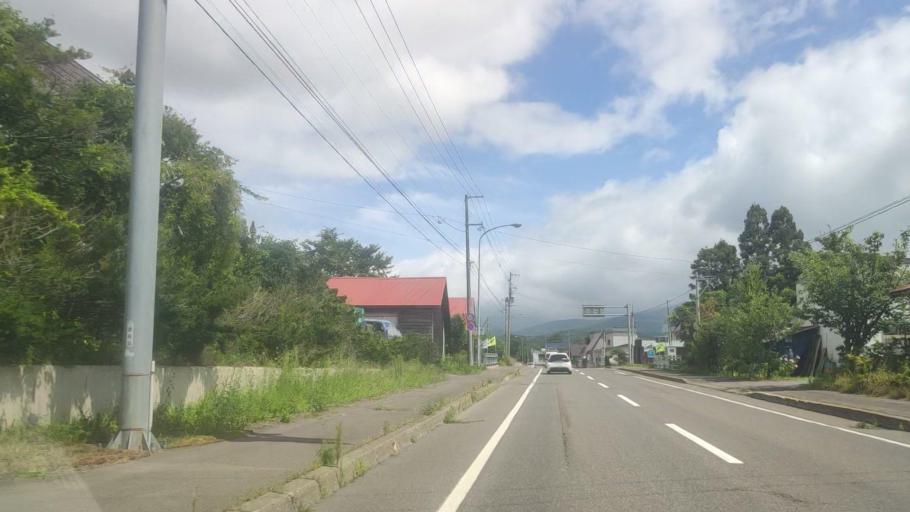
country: JP
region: Hokkaido
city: Date
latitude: 42.5787
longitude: 140.9536
